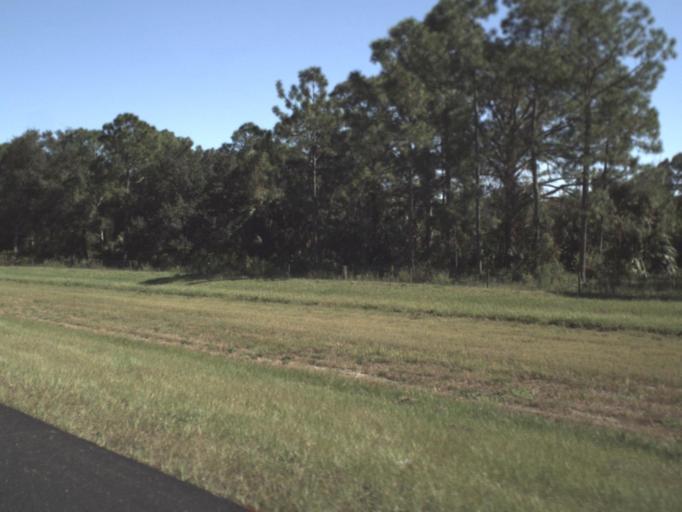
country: US
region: Florida
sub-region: Hendry County
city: Port LaBelle
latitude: 26.7684
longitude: -81.3573
